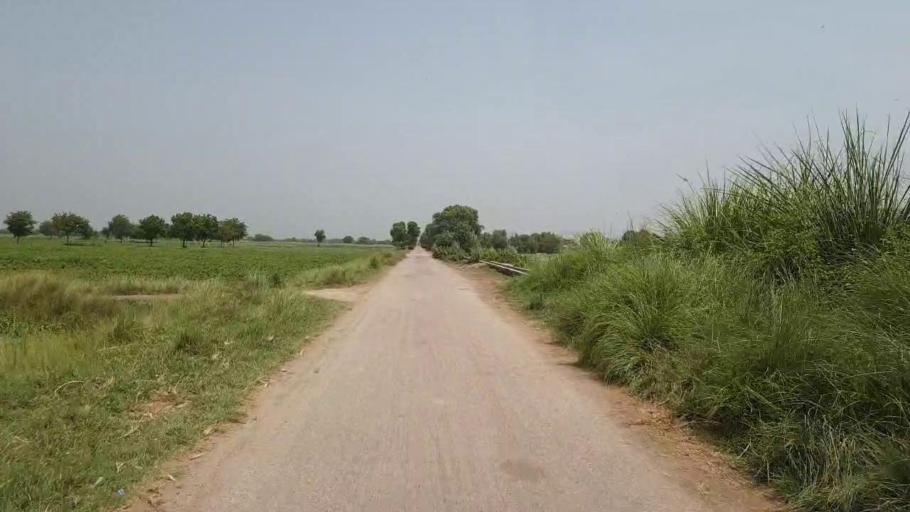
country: PK
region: Sindh
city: Nawabshah
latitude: 26.2890
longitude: 68.3091
